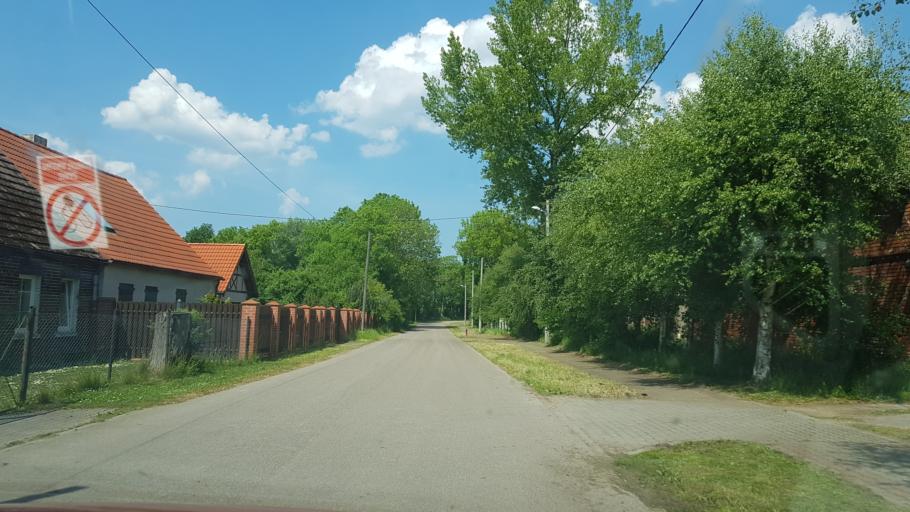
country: PL
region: West Pomeranian Voivodeship
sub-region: Powiat gryficki
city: Trzebiatow
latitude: 54.0874
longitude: 15.2124
